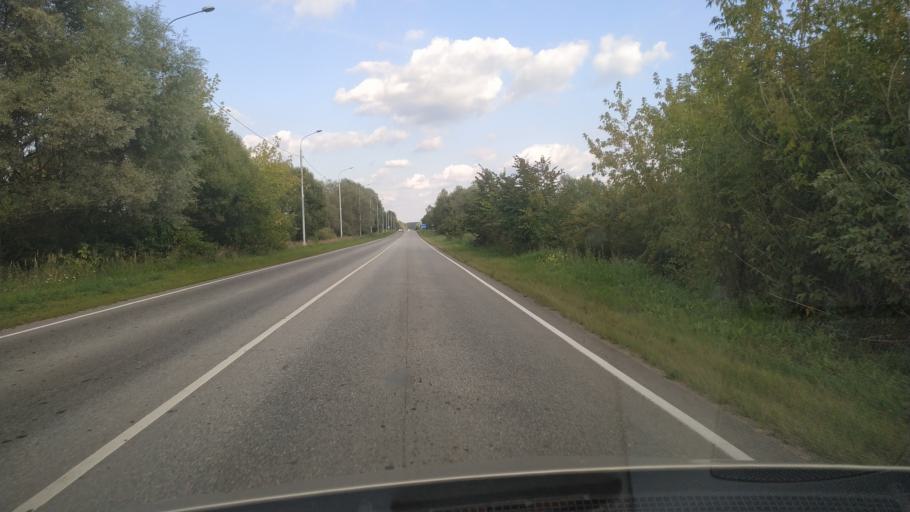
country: RU
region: Moskovskaya
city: Vereya
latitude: 55.7080
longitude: 39.1168
